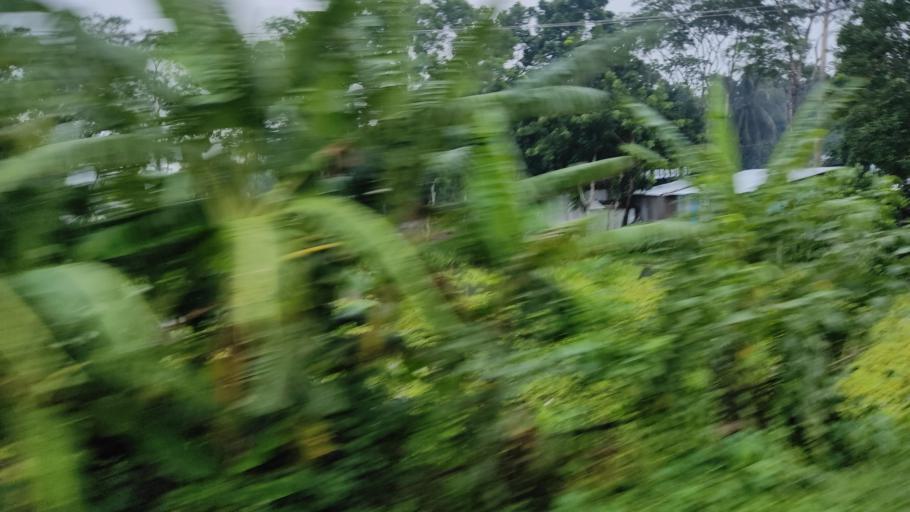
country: BD
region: Barisal
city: Bhandaria
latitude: 22.3175
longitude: 90.3256
